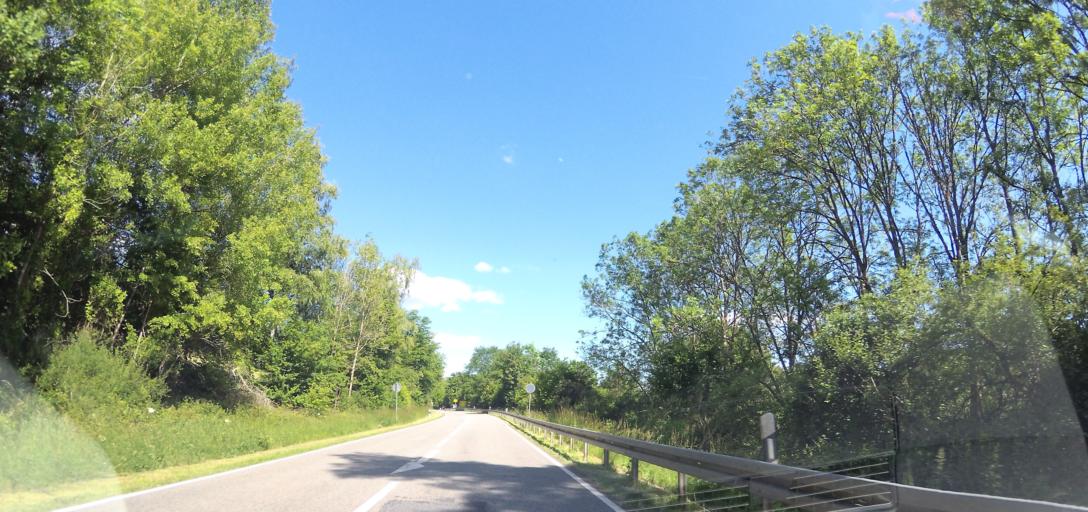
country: DE
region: Saarland
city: Weiskirchen
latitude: 49.5661
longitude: 6.8463
